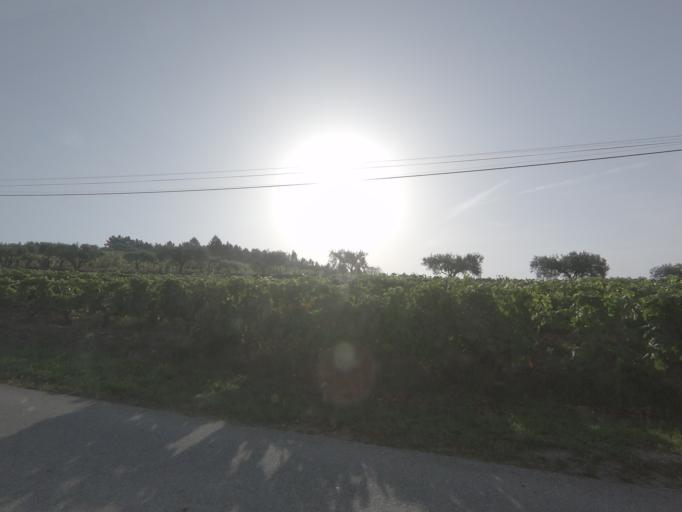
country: PT
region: Vila Real
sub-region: Sabrosa
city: Sabrosa
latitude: 41.2450
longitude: -7.4666
